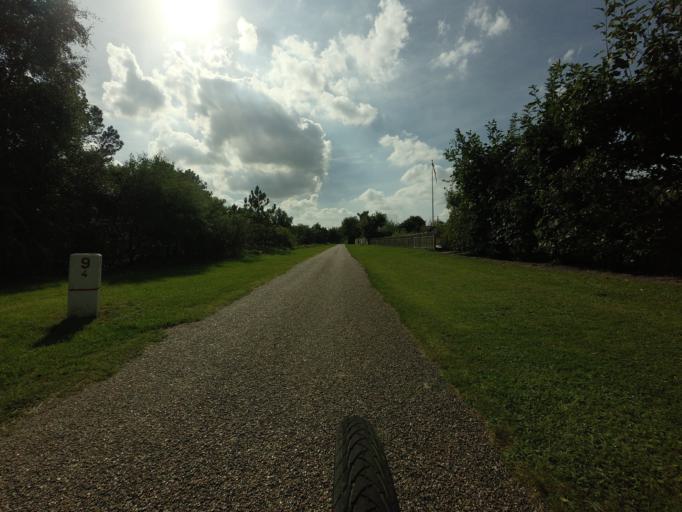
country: DK
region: Central Jutland
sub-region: Herning Kommune
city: Sunds
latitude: 56.2026
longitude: 9.0254
